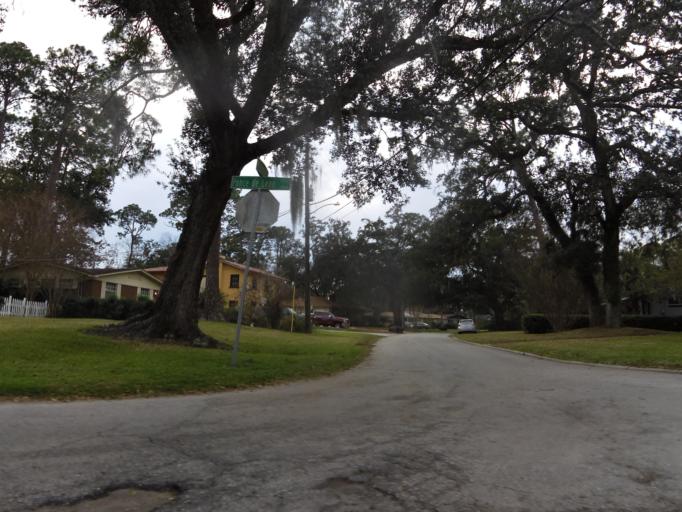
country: US
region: Florida
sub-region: Duval County
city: Jacksonville
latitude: 30.2481
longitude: -81.6307
